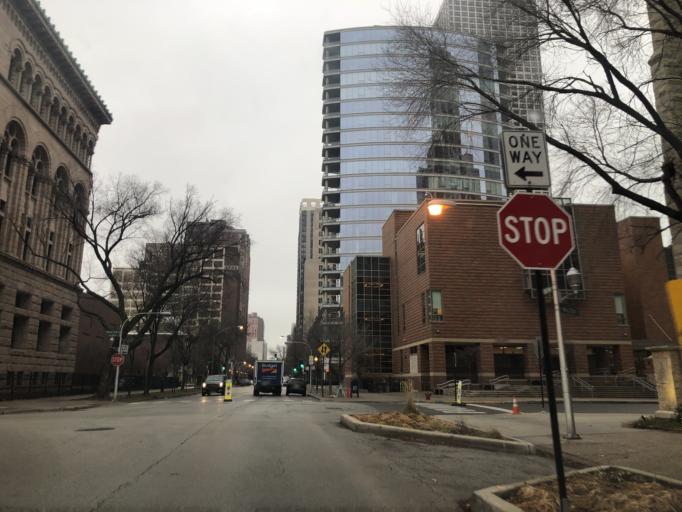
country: US
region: Illinois
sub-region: Cook County
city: Chicago
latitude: 41.8996
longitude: -87.6299
